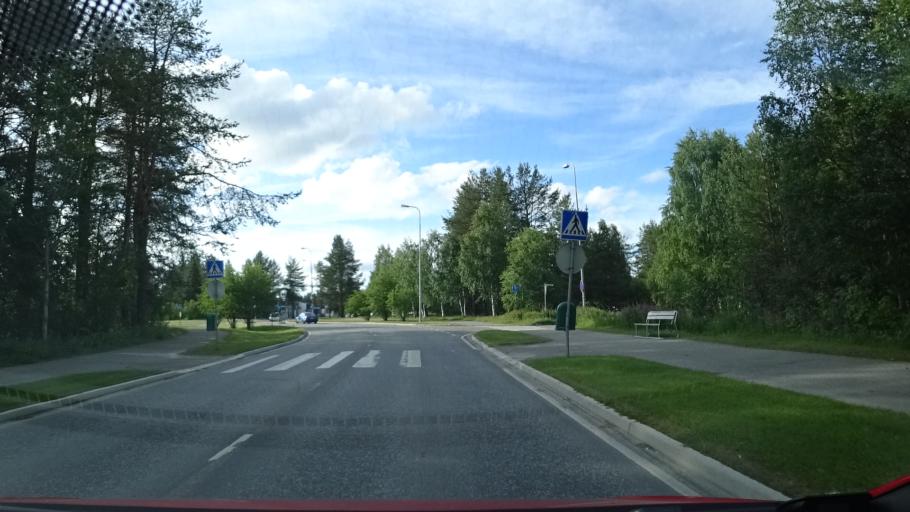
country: FI
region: Lapland
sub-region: Pohjois-Lappi
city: Sodankylae
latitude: 67.4207
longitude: 26.5898
